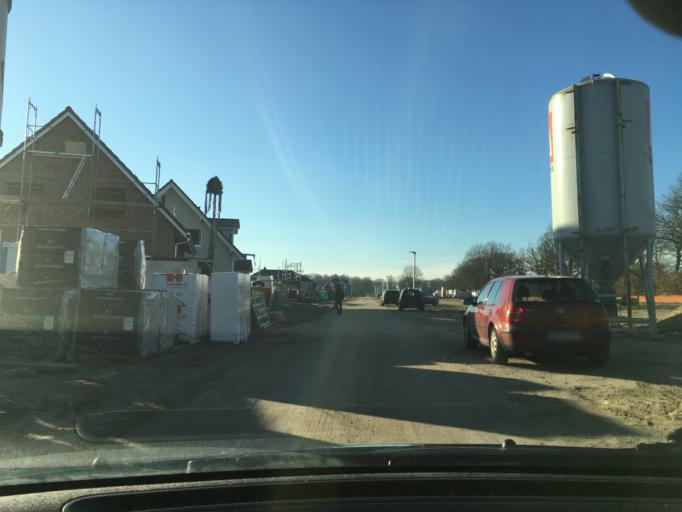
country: DE
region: Schleswig-Holstein
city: Buchen
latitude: 53.4771
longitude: 10.6003
